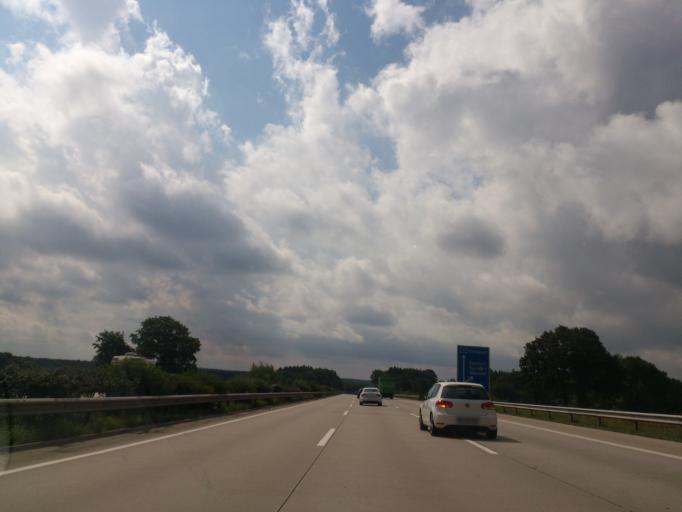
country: DE
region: Lower Saxony
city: Egestorf
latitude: 53.1978
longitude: 10.0805
